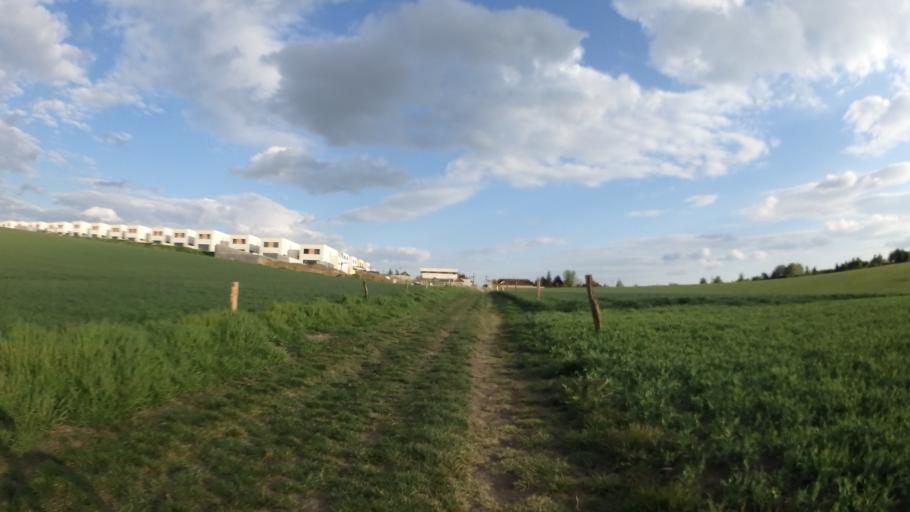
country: CZ
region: South Moravian
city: Moravany
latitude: 49.1524
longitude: 16.5784
